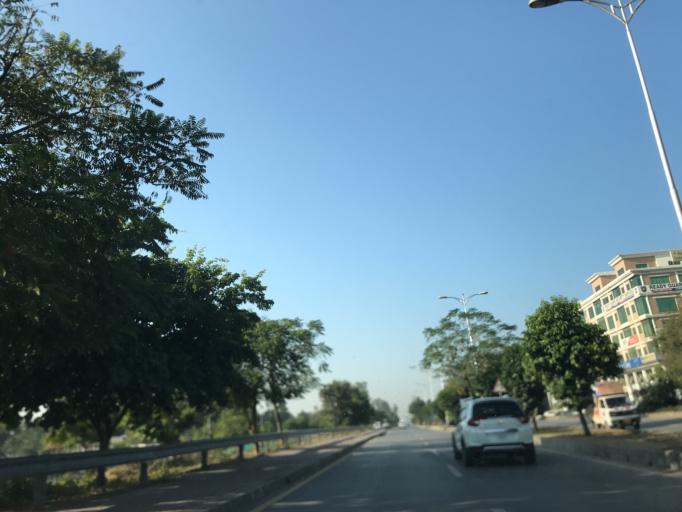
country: PK
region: Islamabad
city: Islamabad
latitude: 33.7194
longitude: 73.0770
